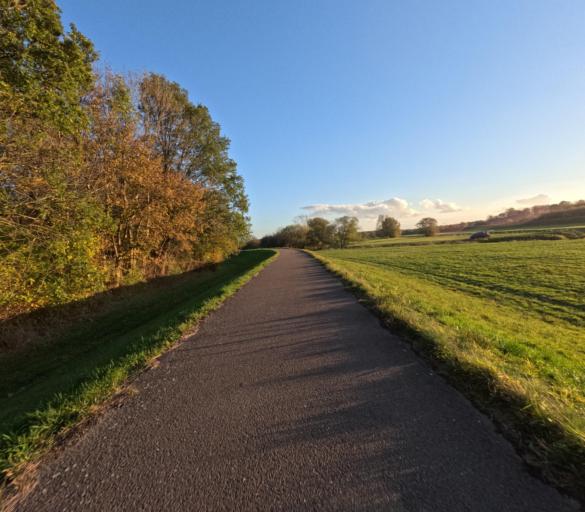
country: DE
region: Saxony-Anhalt
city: Ermlitz
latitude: 51.3832
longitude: 12.1789
